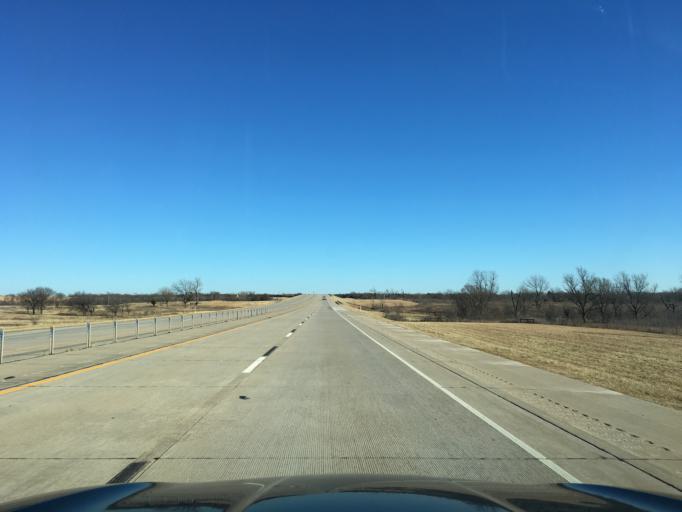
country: US
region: Oklahoma
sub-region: Payne County
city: Yale
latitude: 36.2249
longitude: -96.6930
